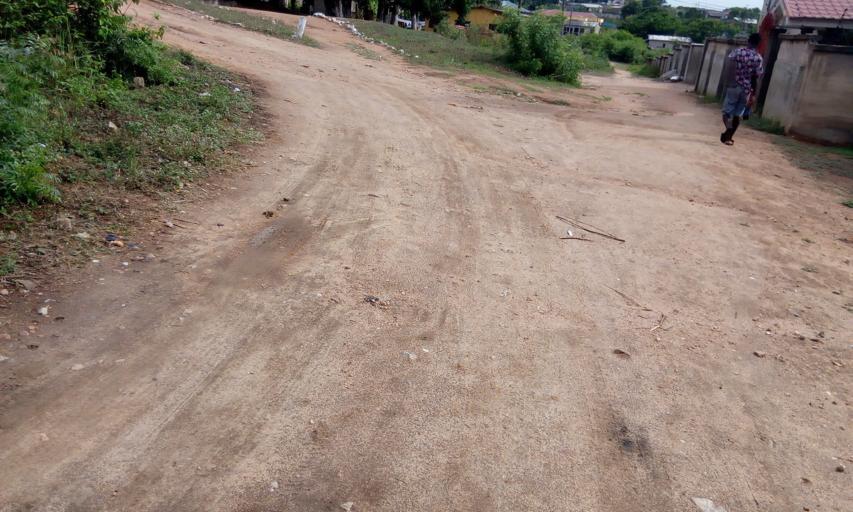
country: GH
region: Central
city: Winneba
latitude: 5.3608
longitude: -0.6199
